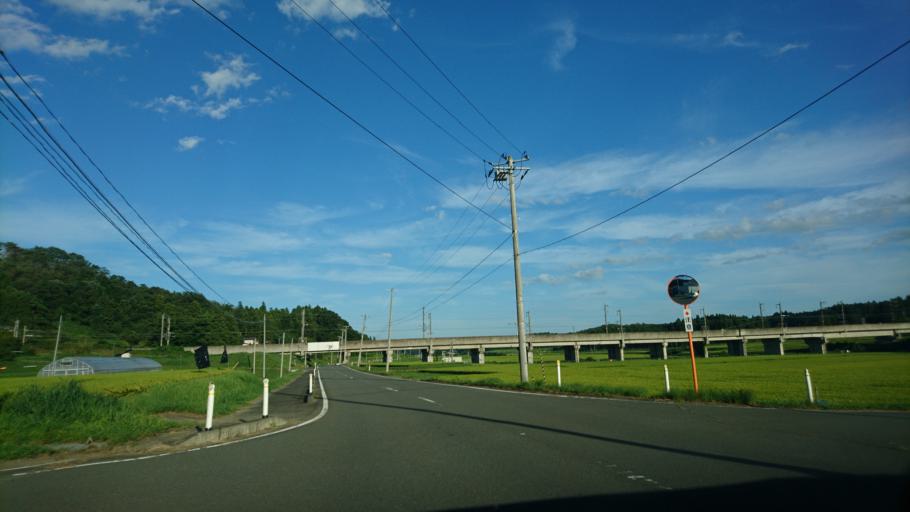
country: JP
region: Iwate
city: Ichinoseki
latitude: 38.8492
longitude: 141.1088
